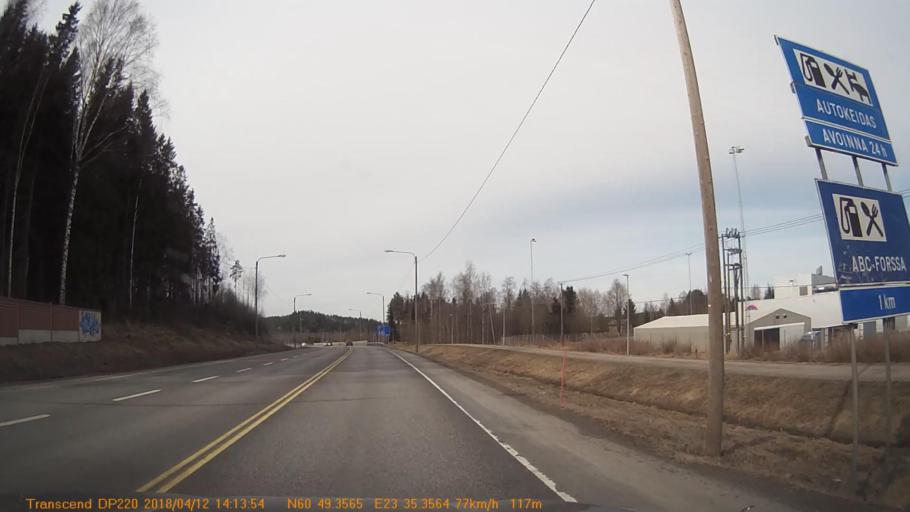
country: FI
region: Haeme
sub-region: Forssa
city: Forssa
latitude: 60.8228
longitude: 23.5890
